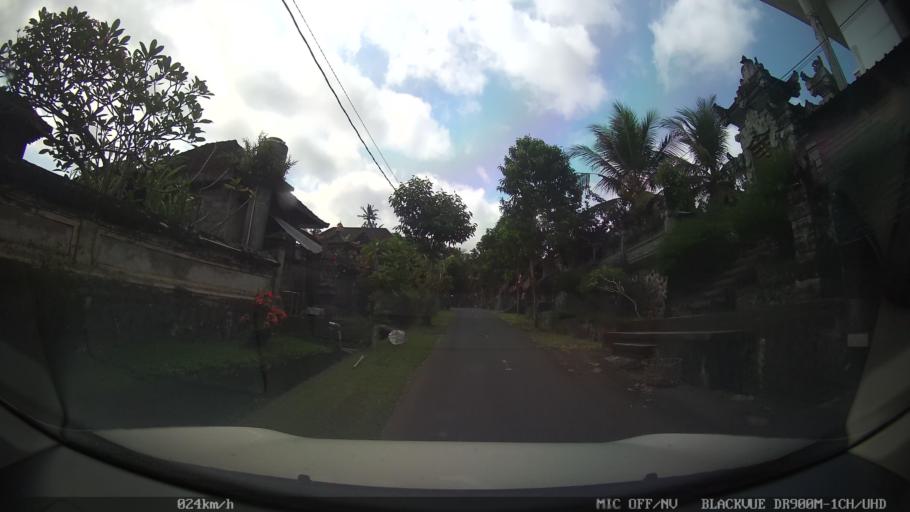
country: ID
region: Bali
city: Banjar Pesalakan
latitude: -8.5137
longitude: 115.3060
